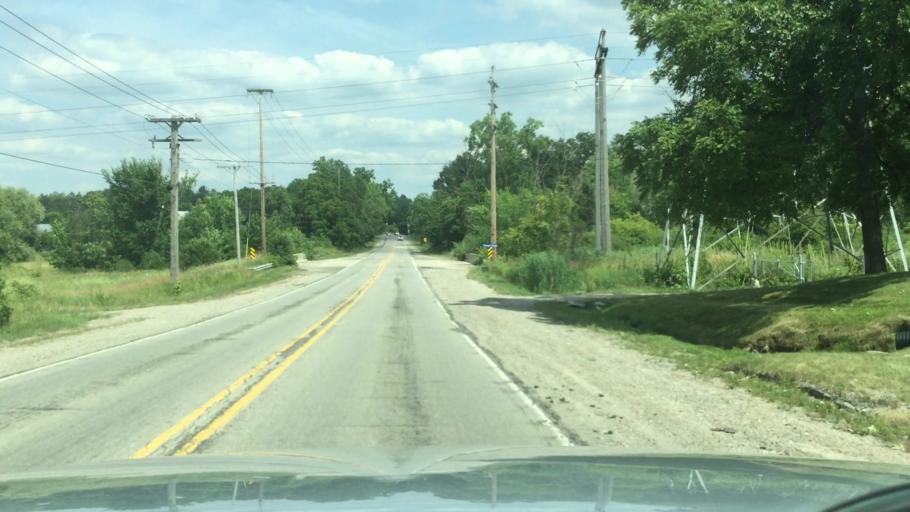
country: US
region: Michigan
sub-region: Genesee County
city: Grand Blanc
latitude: 42.9447
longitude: -83.6470
